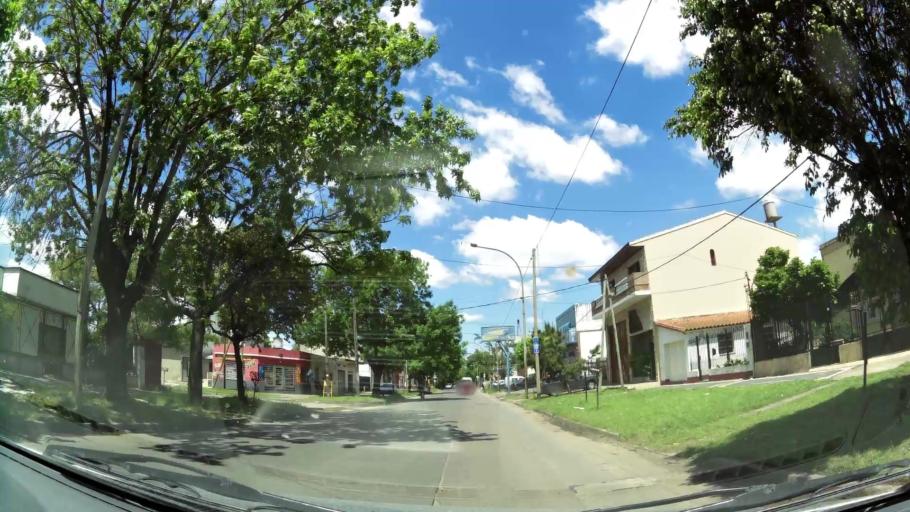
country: AR
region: Buenos Aires
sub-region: Partido de Lanus
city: Lanus
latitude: -34.7227
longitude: -58.4094
